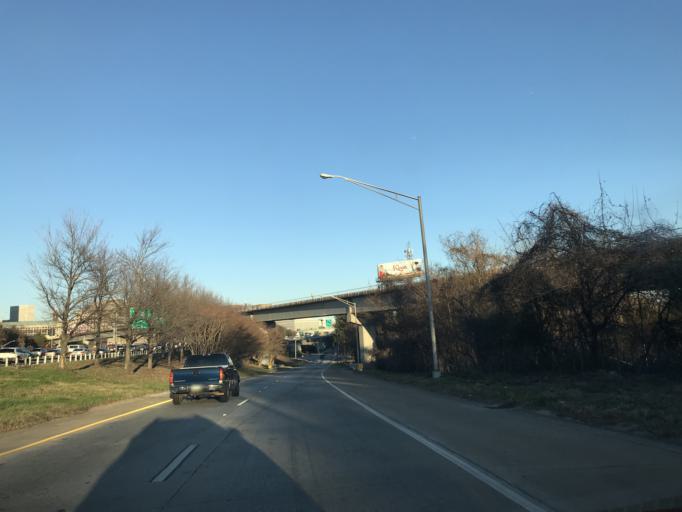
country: US
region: Georgia
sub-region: Fulton County
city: Atlanta
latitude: 33.7437
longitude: -84.4009
